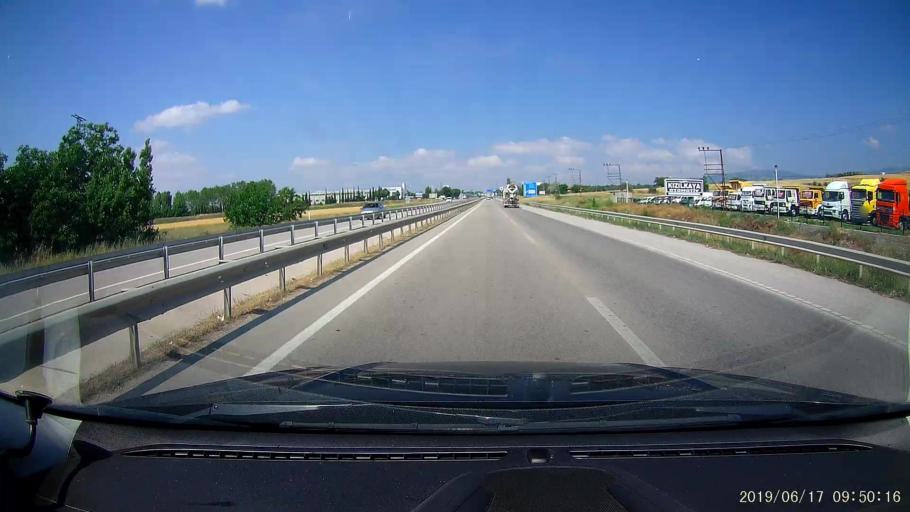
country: TR
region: Amasya
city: Merzifon
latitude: 40.8713
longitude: 35.5110
